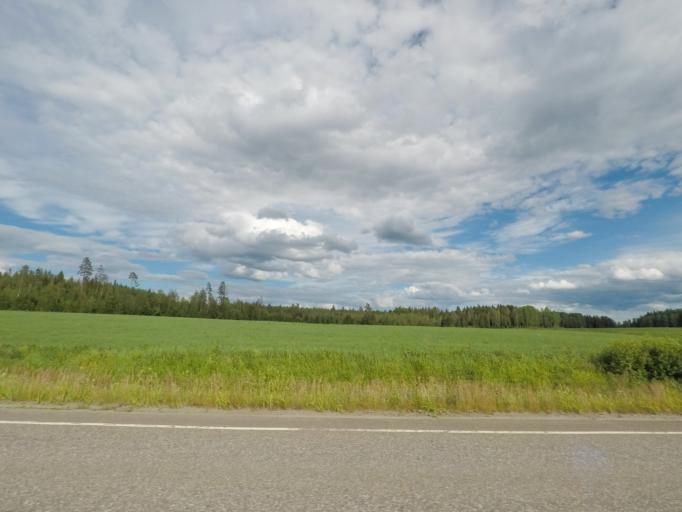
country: FI
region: Paijanne Tavastia
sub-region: Lahti
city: Hollola
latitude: 60.8248
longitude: 25.4878
